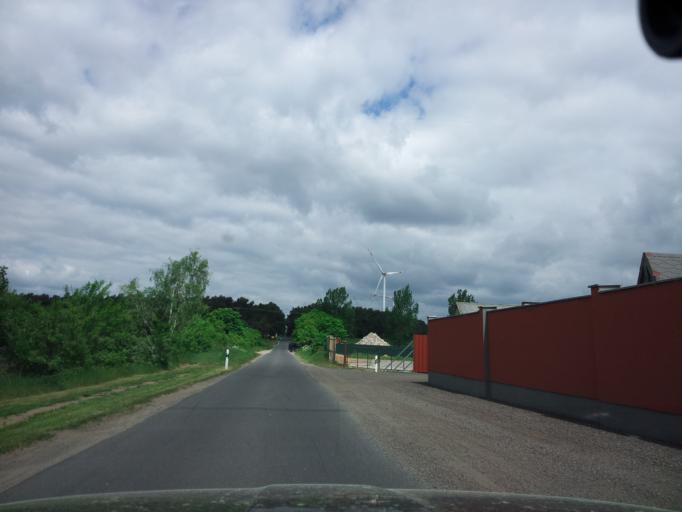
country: DE
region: Brandenburg
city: Treuenbrietzen
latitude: 52.0773
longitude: 12.8069
